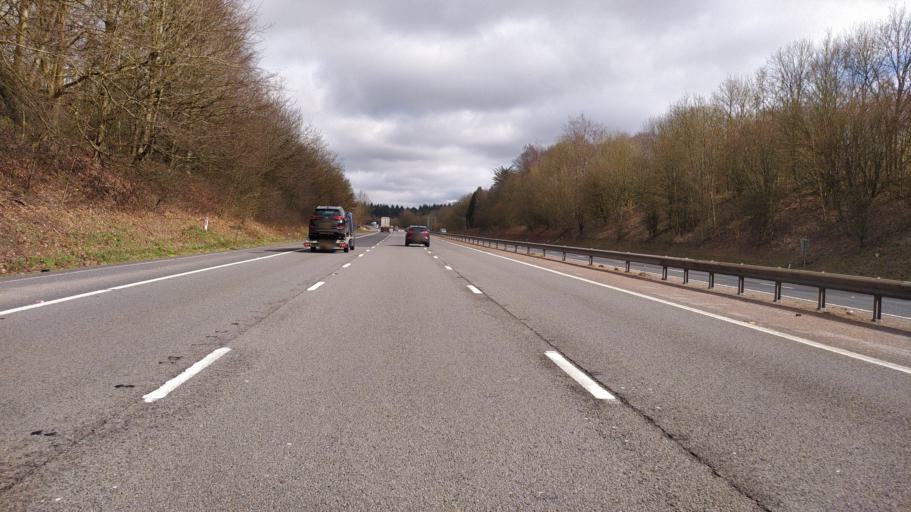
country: GB
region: England
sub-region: Hampshire
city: Basingstoke
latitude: 51.2228
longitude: -1.1438
